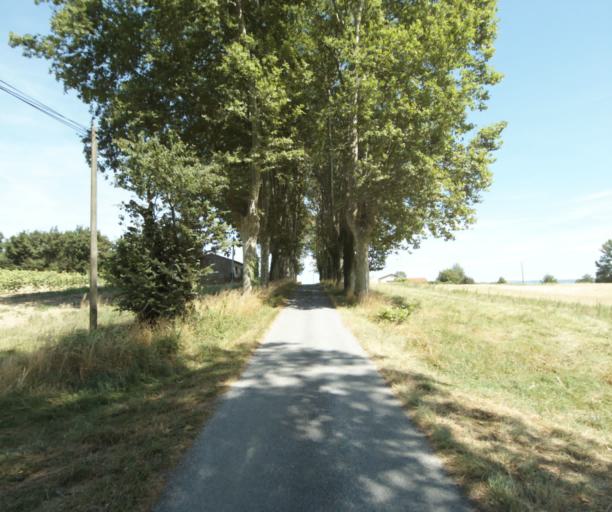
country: FR
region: Midi-Pyrenees
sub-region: Departement du Tarn
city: Puylaurens
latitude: 43.5334
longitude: 2.0084
